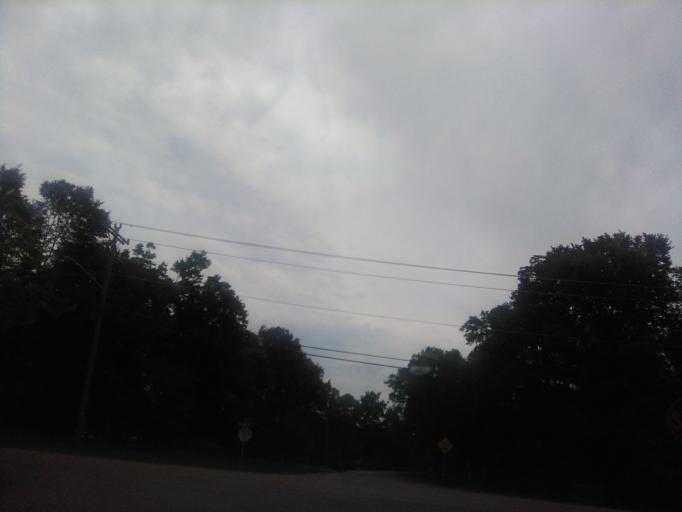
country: US
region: Tennessee
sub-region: Davidson County
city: Belle Meade
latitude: 36.1124
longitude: -86.8909
